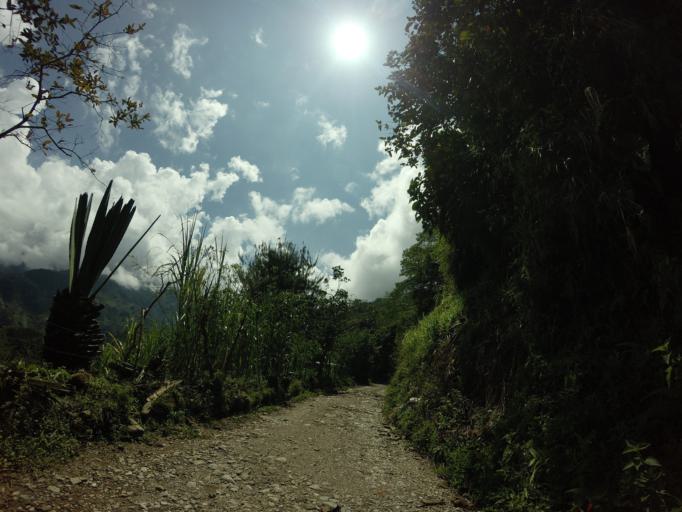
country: CO
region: Caldas
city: Pensilvania
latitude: 5.4778
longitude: -75.1871
